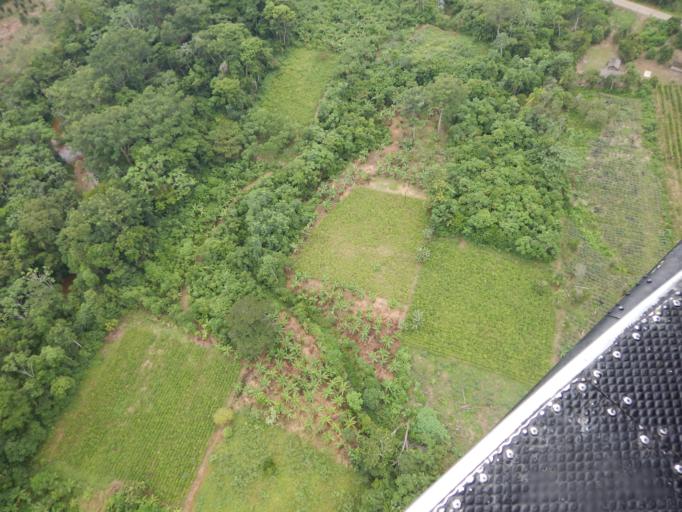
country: BO
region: Cochabamba
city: Chimore
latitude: -17.1560
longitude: -64.7898
